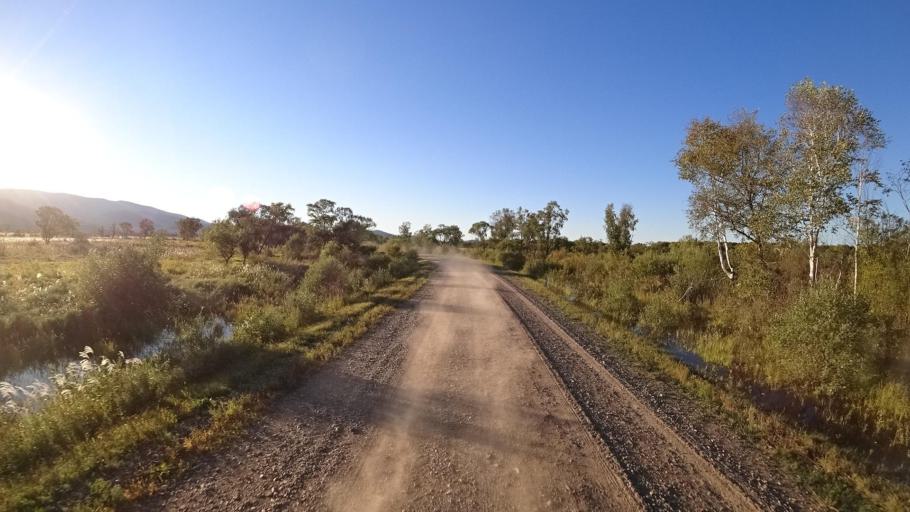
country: RU
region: Primorskiy
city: Kirovskiy
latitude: 44.8139
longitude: 133.6151
